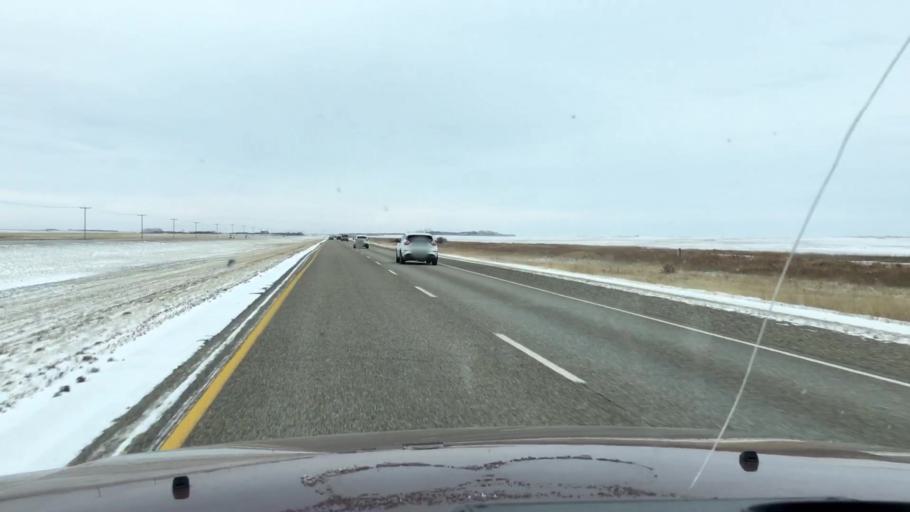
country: CA
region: Saskatchewan
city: Moose Jaw
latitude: 50.9963
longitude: -105.7593
